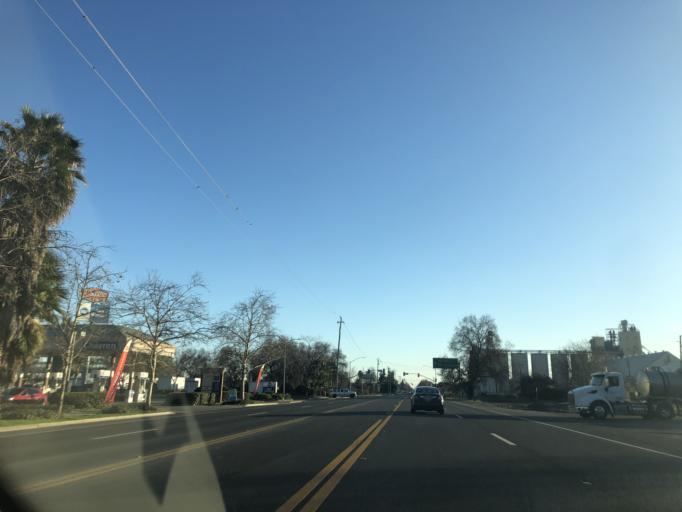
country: US
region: California
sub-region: Yolo County
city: Woodland
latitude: 38.6962
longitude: -121.7653
